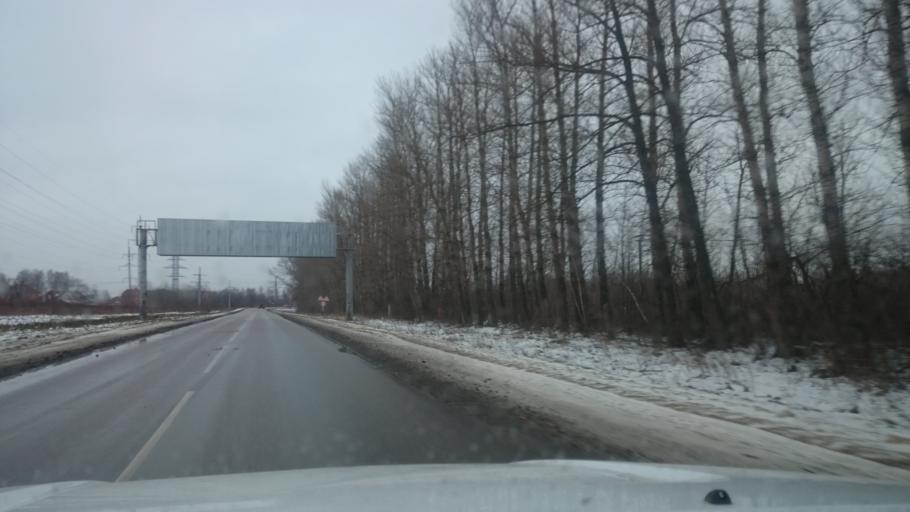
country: RU
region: Tula
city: Kosaya Gora
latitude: 54.1816
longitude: 37.5110
